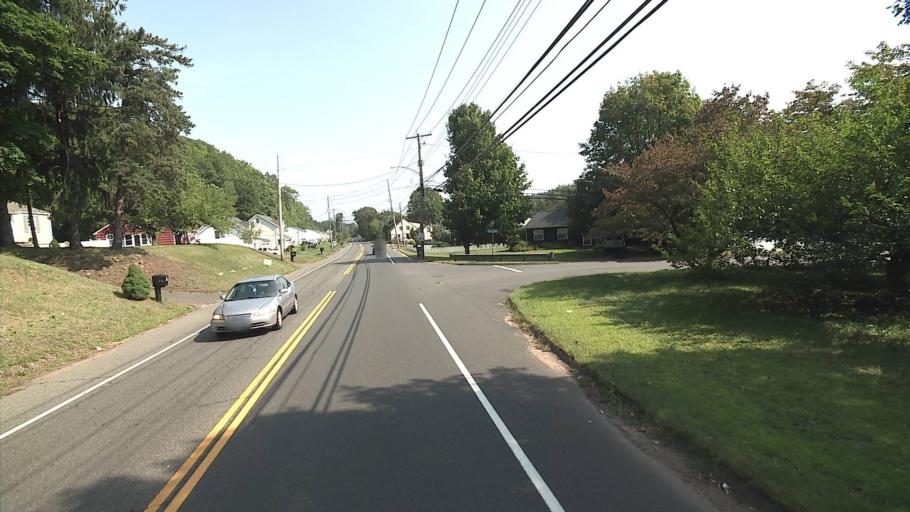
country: US
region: Connecticut
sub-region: New Haven County
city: East Haven
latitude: 41.3066
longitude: -72.8524
